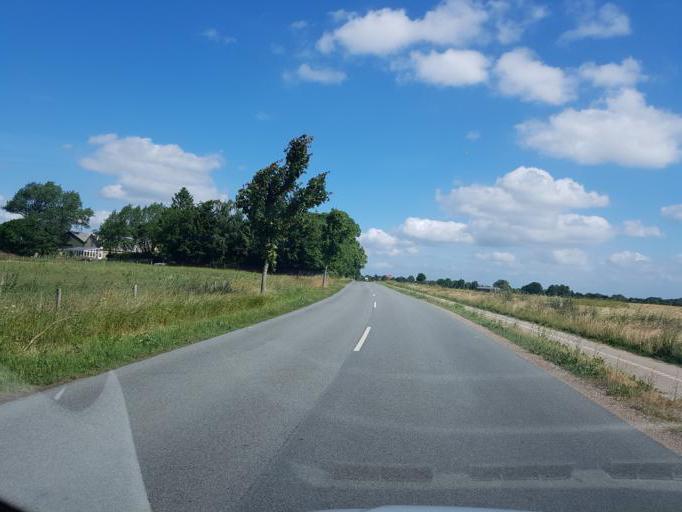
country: DK
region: Zealand
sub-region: Lejre Kommune
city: Lejre
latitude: 55.5877
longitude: 11.9693
